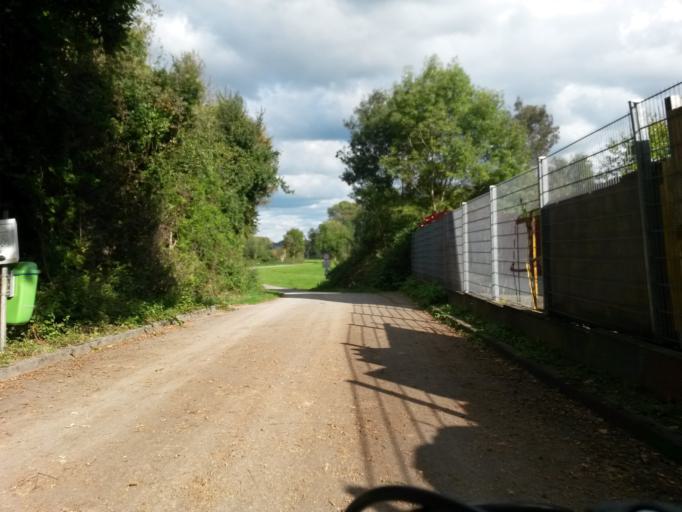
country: DE
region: Baden-Wuerttemberg
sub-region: Regierungsbezirk Stuttgart
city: Oberriexingen
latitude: 48.9319
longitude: 9.0346
